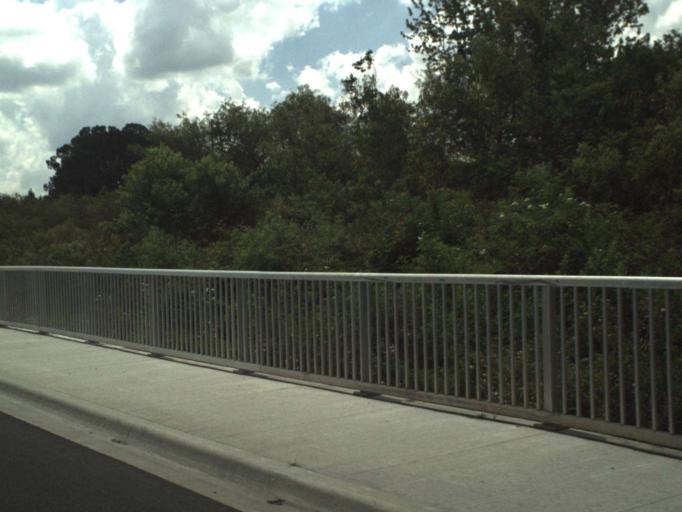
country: US
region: Florida
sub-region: Seminole County
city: Longwood
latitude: 28.6977
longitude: -81.3708
